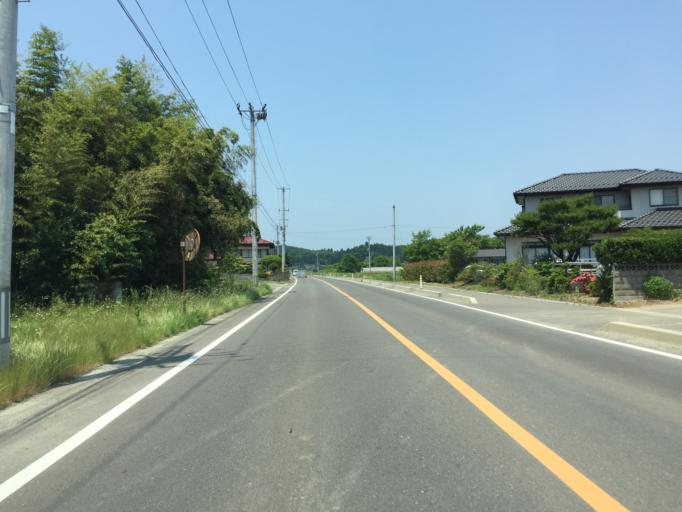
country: JP
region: Miyagi
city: Marumori
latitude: 37.8853
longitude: 140.8177
